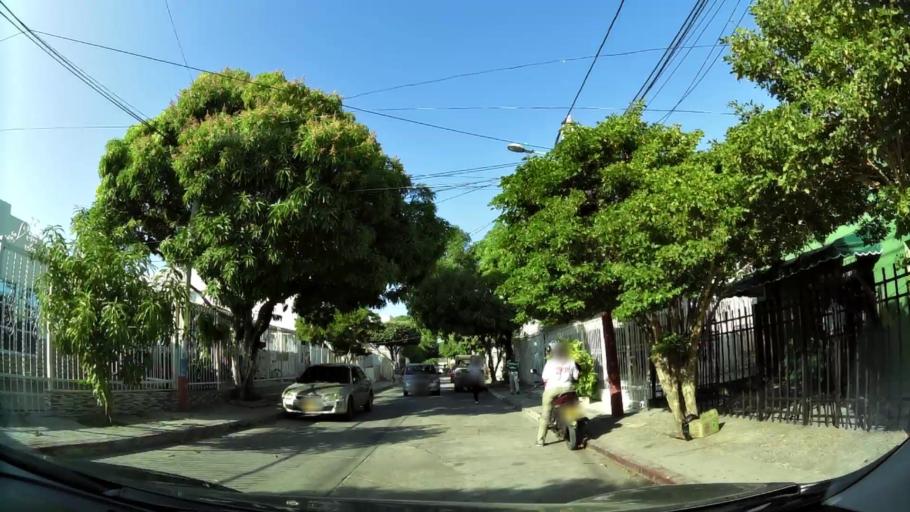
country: CO
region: Bolivar
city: Cartagena
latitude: 10.3855
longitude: -75.4829
